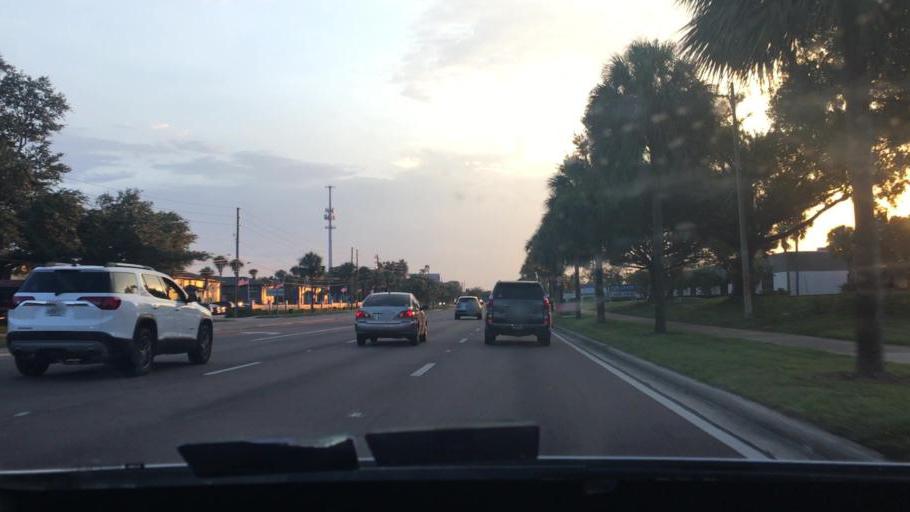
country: US
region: Florida
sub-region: Seminole County
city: Goldenrod
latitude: 28.5976
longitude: -81.2922
